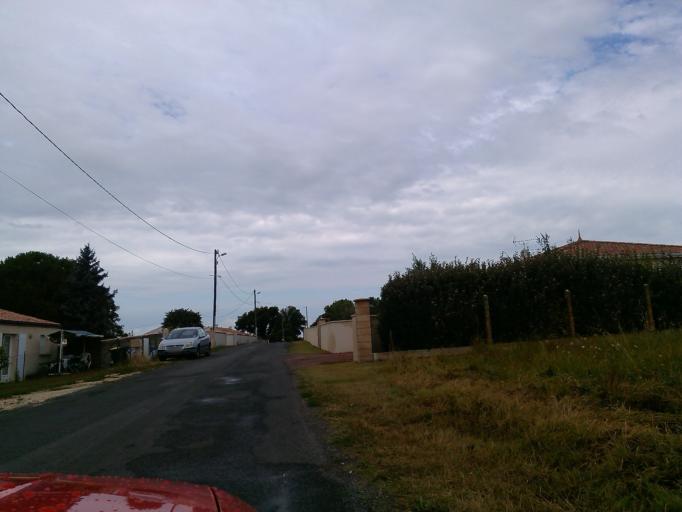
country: FR
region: Poitou-Charentes
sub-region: Departement de la Charente-Maritime
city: Arvert
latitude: 45.7386
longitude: -1.1315
